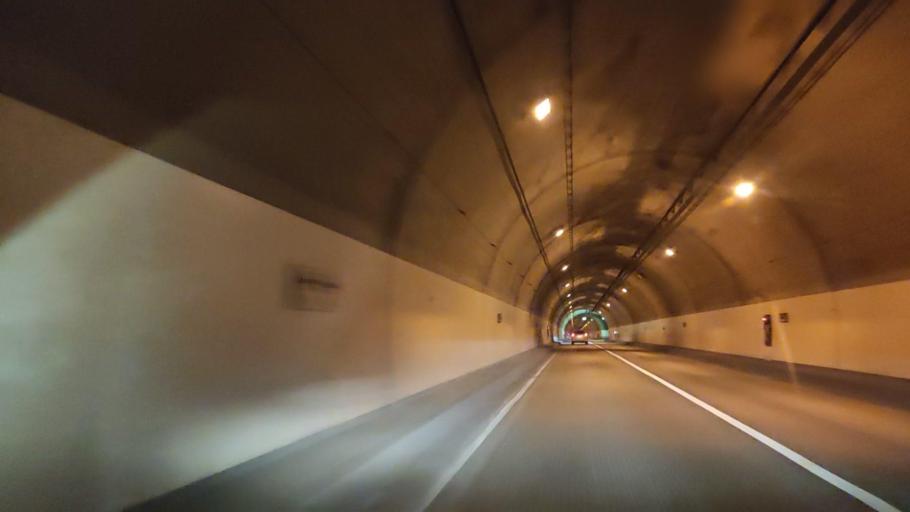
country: JP
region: Hokkaido
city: Ishikari
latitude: 43.4608
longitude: 141.4048
